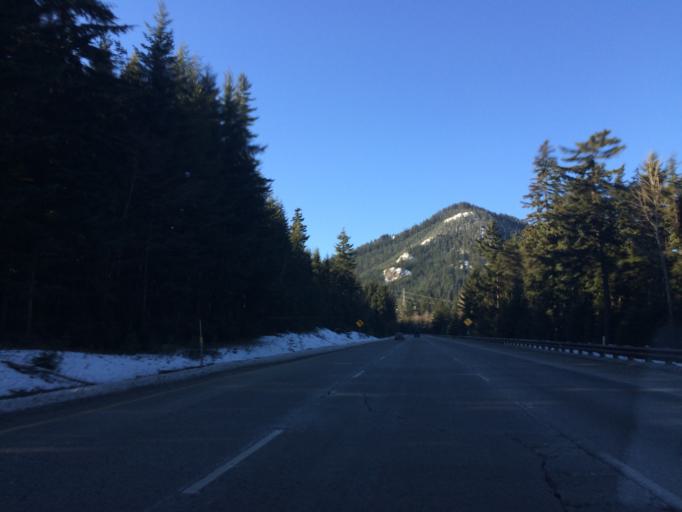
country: US
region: Washington
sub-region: Kittitas County
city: Cle Elum
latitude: 47.2667
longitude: -121.2248
